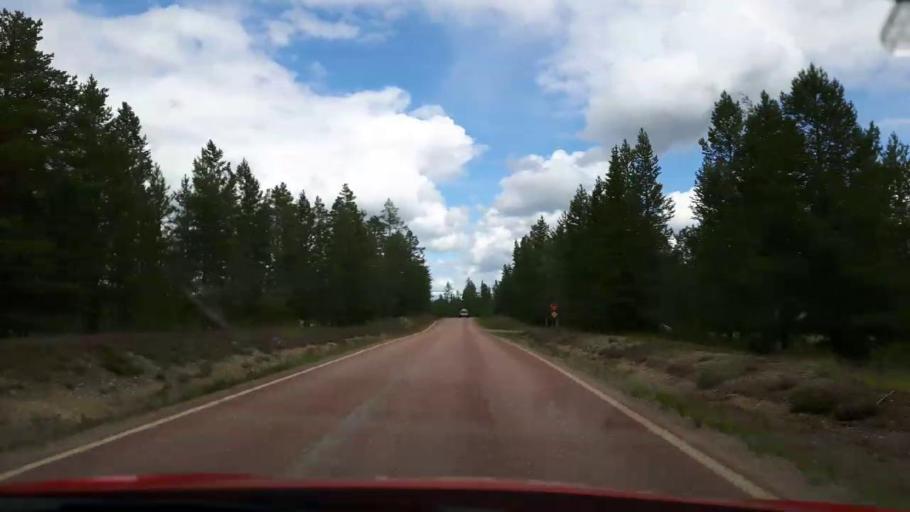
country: NO
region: Hedmark
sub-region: Trysil
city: Innbygda
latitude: 61.8895
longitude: 12.9831
